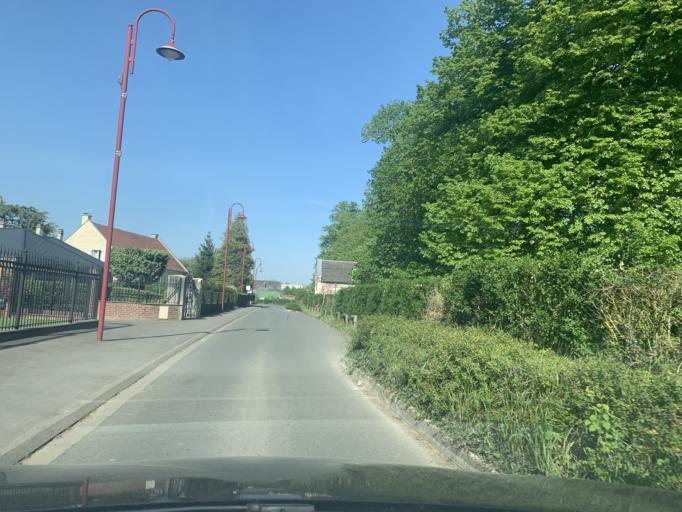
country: FR
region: Nord-Pas-de-Calais
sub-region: Departement du Nord
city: Proville
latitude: 50.1697
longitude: 3.2160
